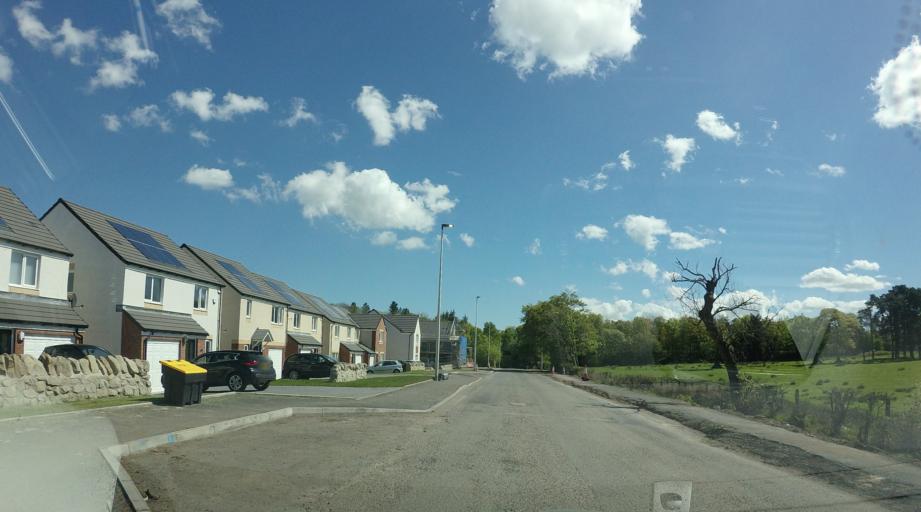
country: GB
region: Scotland
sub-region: Falkirk
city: Polmont
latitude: 55.9725
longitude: -3.6897
